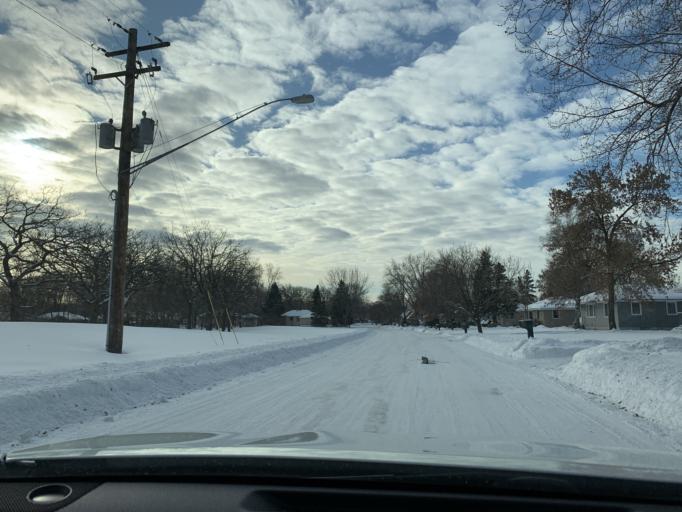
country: US
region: Minnesota
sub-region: Anoka County
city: Blaine
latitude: 45.1767
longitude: -93.2854
